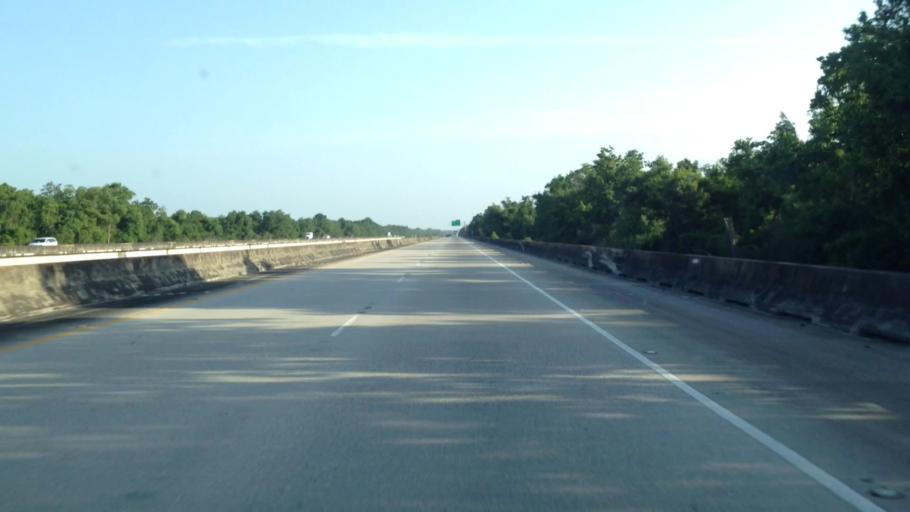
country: US
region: Louisiana
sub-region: Tangipahoa Parish
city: Ponchatoula
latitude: 30.3780
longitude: -90.4242
